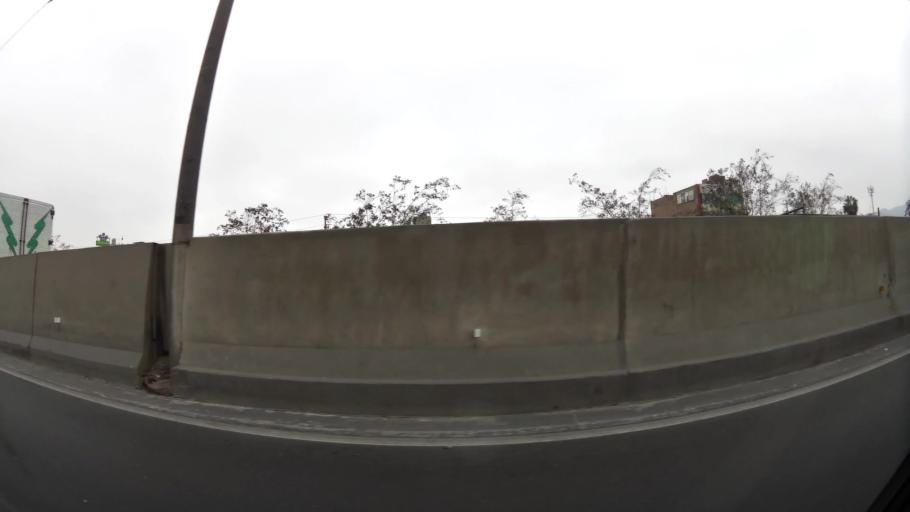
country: PE
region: Lima
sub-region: Lima
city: Independencia
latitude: -11.9346
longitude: -77.0720
